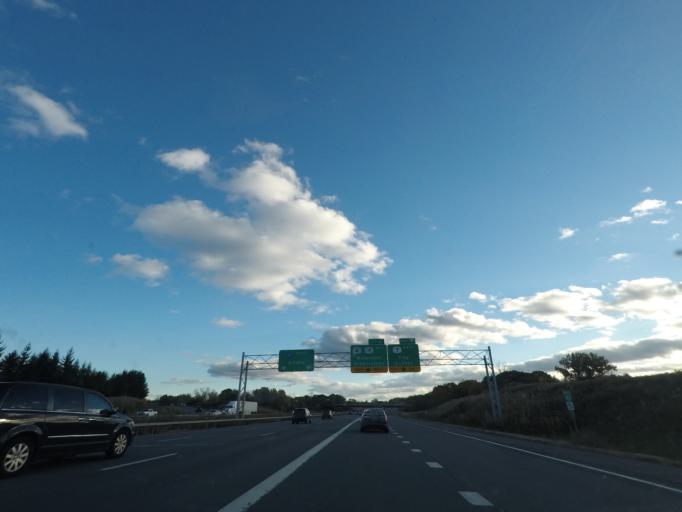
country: US
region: New York
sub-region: Albany County
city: Cohoes
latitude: 42.7676
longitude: -73.7621
